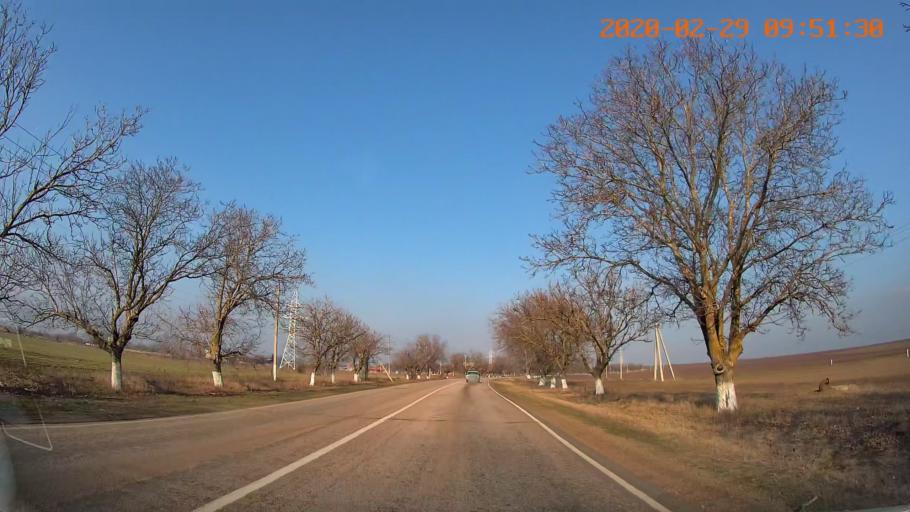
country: MD
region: Telenesti
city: Slobozia
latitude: 46.7090
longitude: 29.7388
